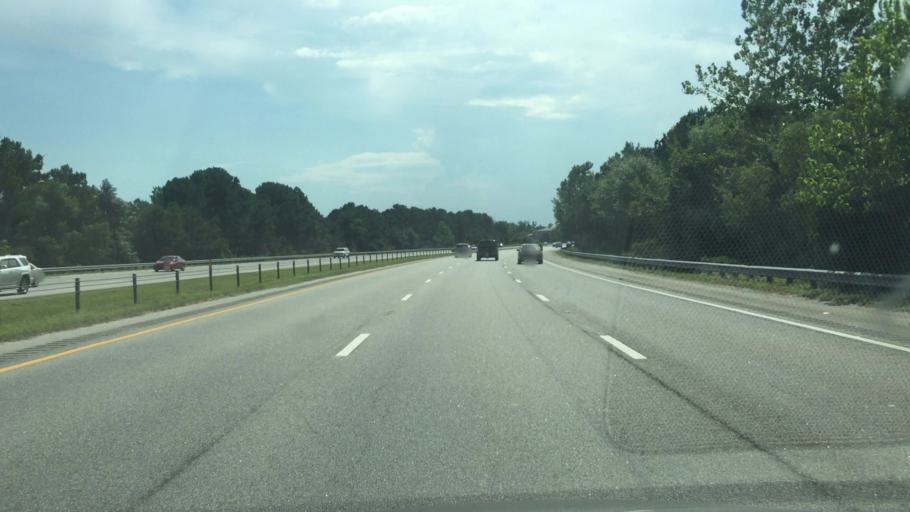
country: US
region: South Carolina
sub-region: Horry County
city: North Myrtle Beach
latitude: 33.8168
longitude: -78.7415
